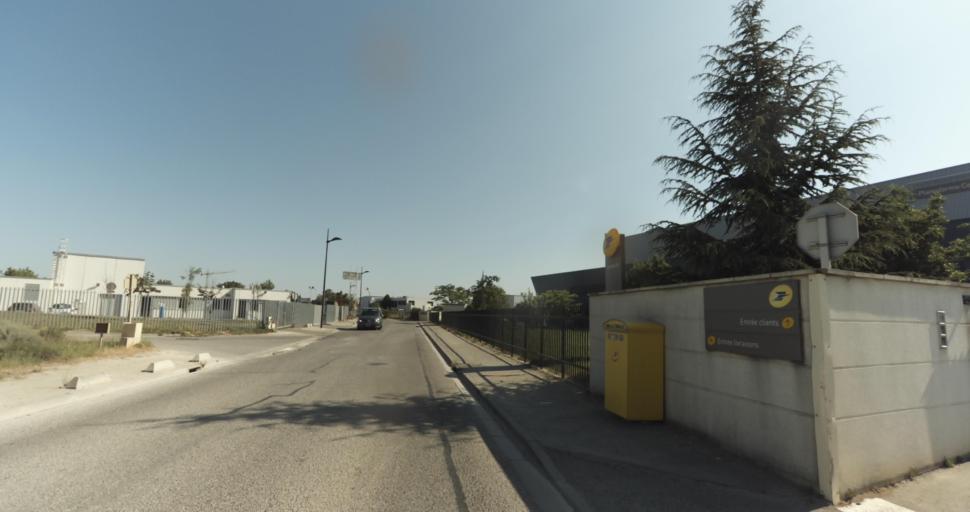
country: FR
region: Midi-Pyrenees
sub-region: Departement de la Haute-Garonne
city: Tournefeuille
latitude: 43.5931
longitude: 1.3001
